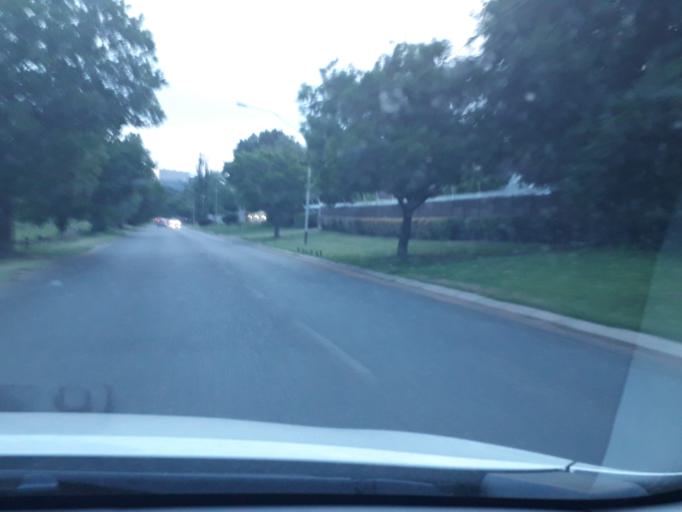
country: ZA
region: Gauteng
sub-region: City of Johannesburg Metropolitan Municipality
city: Johannesburg
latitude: -26.1462
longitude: 27.9993
